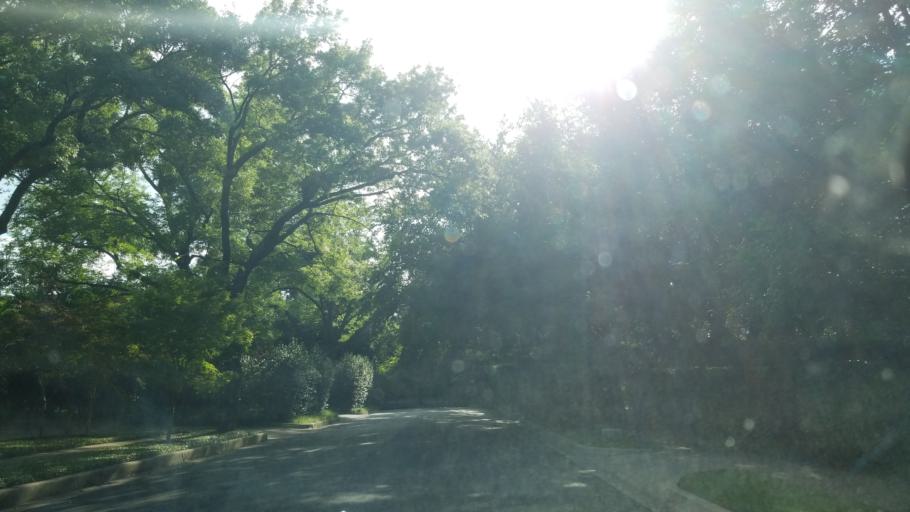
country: US
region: Texas
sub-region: Dallas County
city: Highland Park
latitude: 32.8401
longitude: -96.7983
